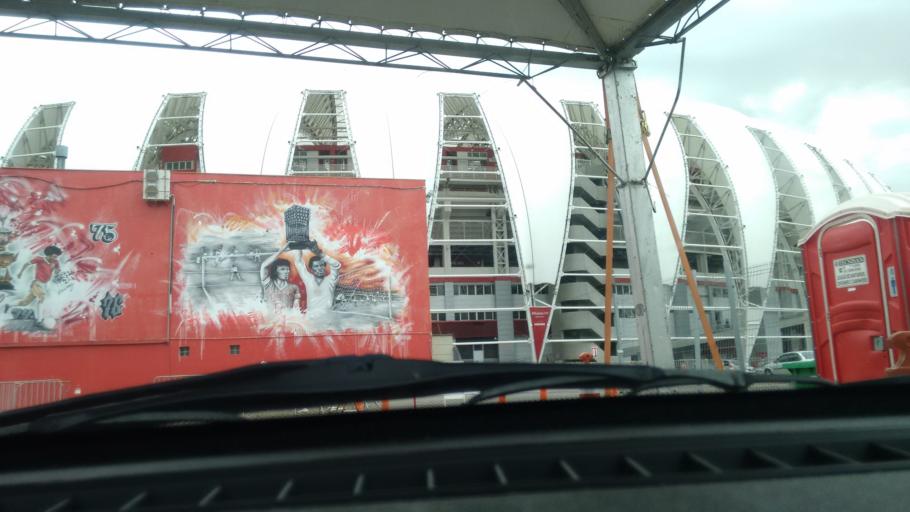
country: BR
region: Rio Grande do Sul
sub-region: Porto Alegre
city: Porto Alegre
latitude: -30.0638
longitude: -51.2354
